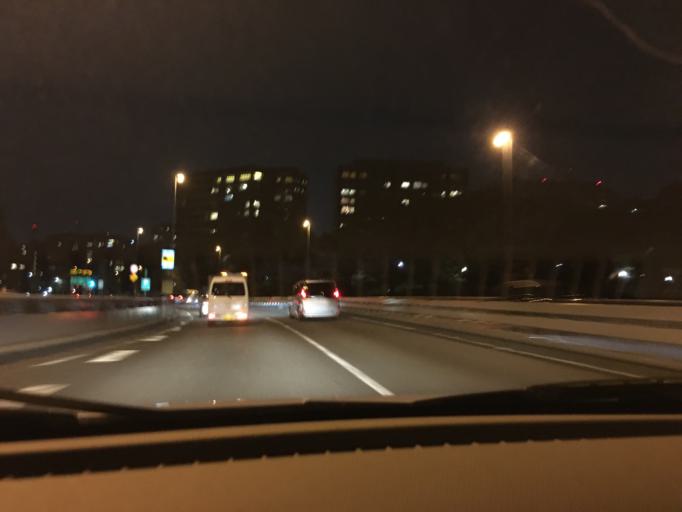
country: JP
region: Tokyo
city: Tokyo
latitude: 35.6894
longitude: 139.7486
